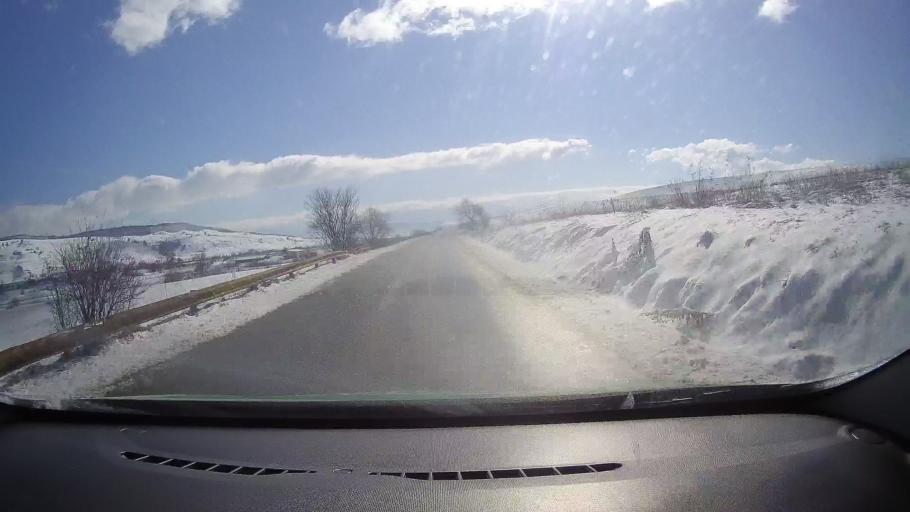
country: RO
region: Sibiu
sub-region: Comuna Rosia
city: Rosia
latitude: 45.8339
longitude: 24.3104
